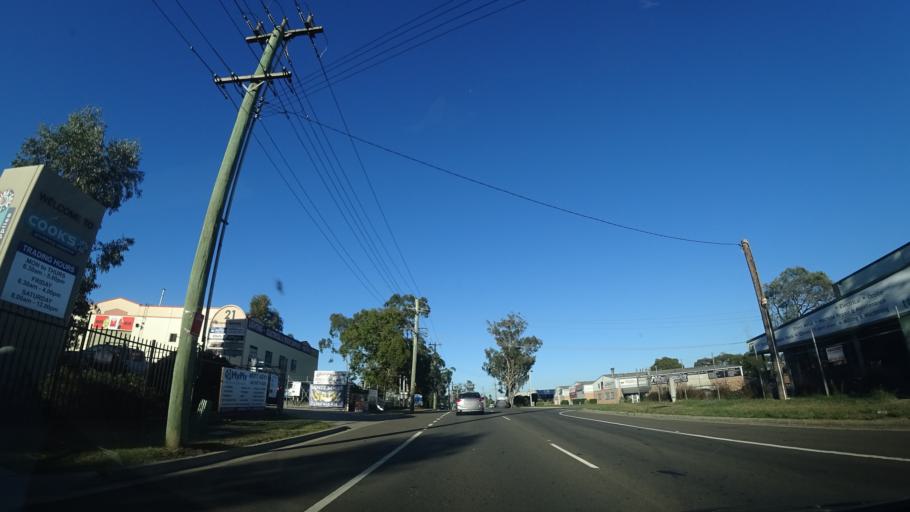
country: AU
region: New South Wales
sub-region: Hawkesbury
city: South Windsor
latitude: -33.6268
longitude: 150.8366
